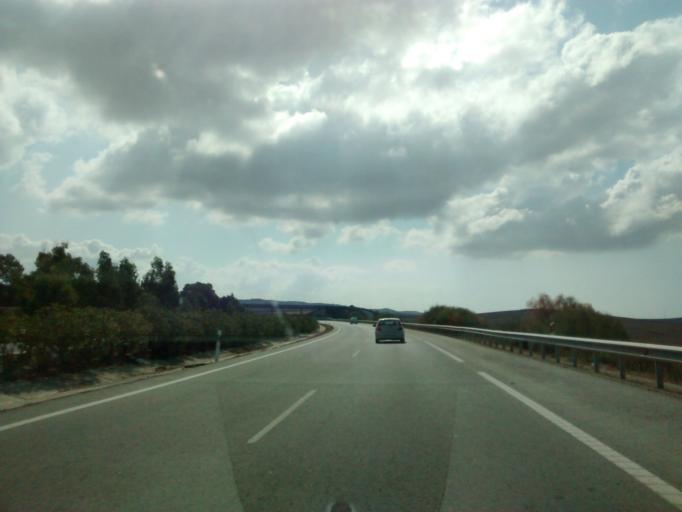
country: ES
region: Andalusia
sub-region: Provincia de Cadiz
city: Vejer de la Frontera
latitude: 36.2519
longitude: -6.0251
